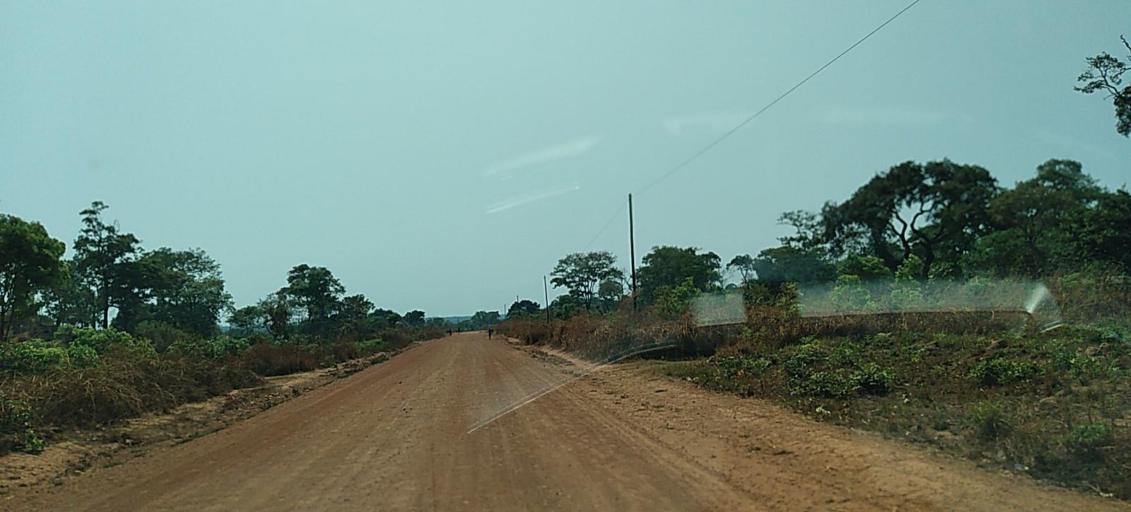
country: ZM
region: North-Western
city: Kansanshi
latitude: -11.9973
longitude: 26.6086
